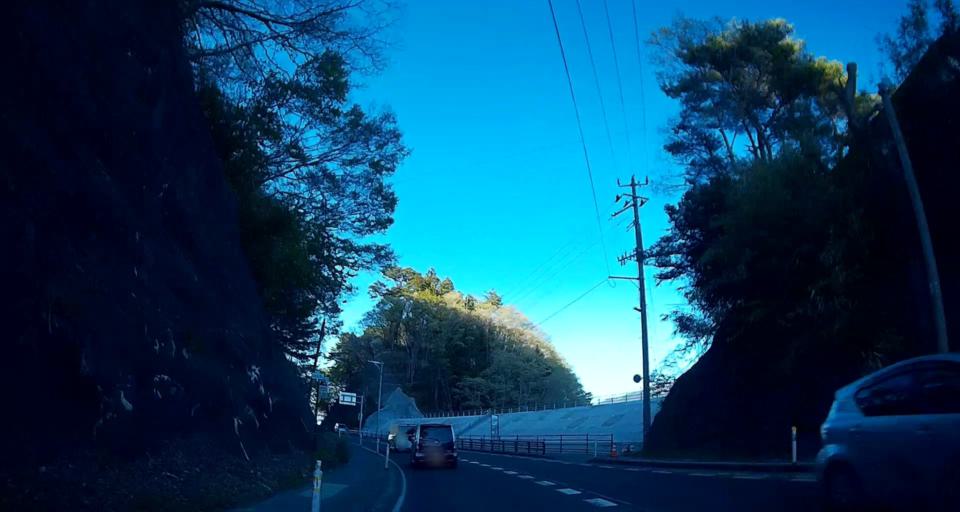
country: JP
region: Iwate
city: Miyako
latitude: 39.6101
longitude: 141.9609
